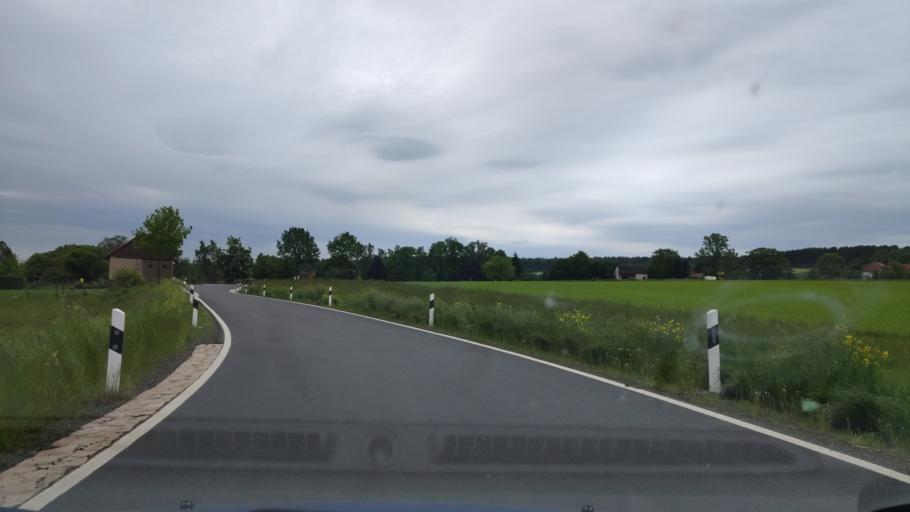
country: DE
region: Lower Saxony
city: Hardegsen
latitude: 51.7037
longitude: 9.7831
